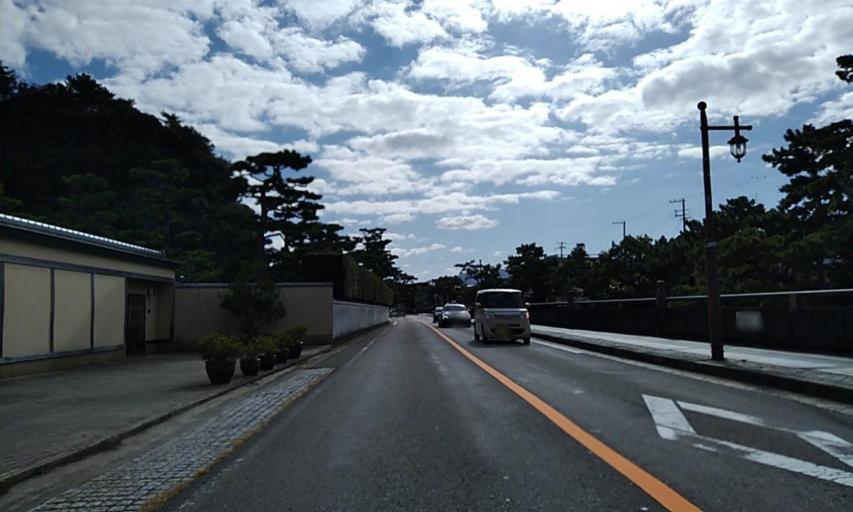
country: JP
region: Wakayama
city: Minato
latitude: 34.1880
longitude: 135.1701
